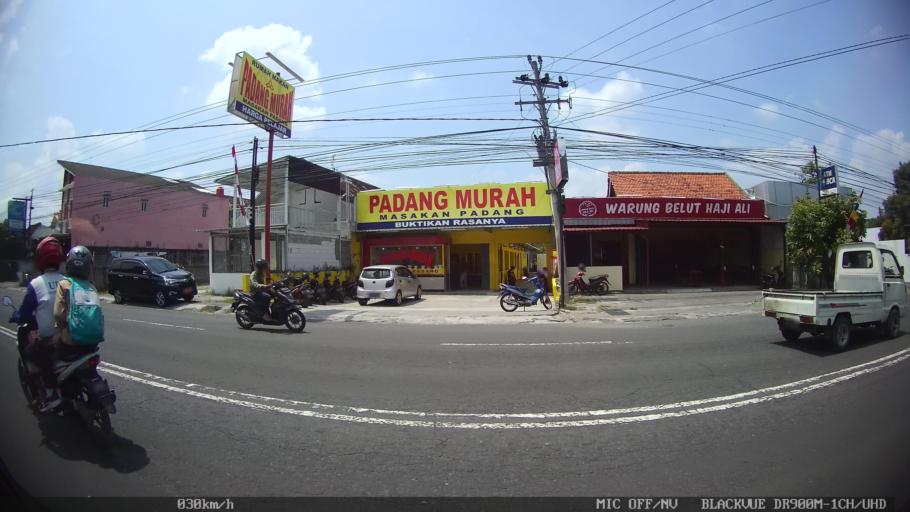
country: ID
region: Daerah Istimewa Yogyakarta
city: Yogyakarta
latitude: -7.8165
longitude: 110.4020
